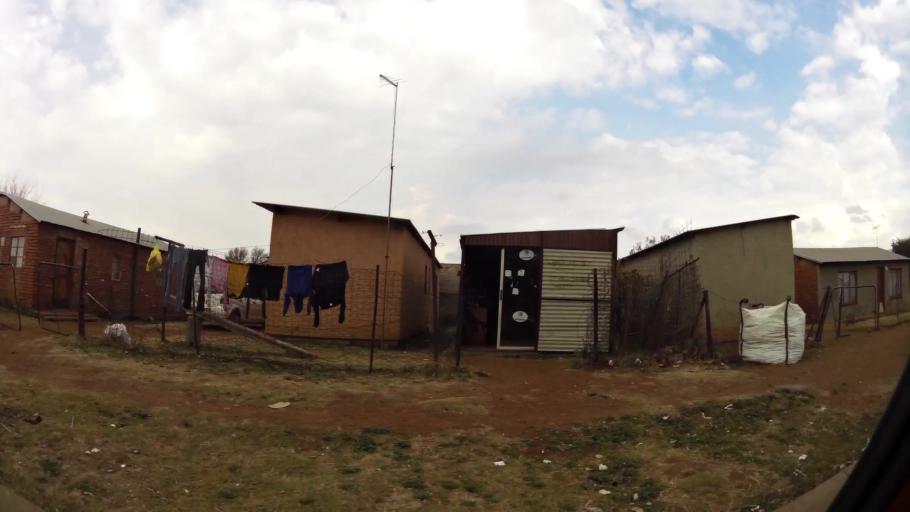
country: ZA
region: Gauteng
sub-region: Sedibeng District Municipality
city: Vanderbijlpark
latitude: -26.6637
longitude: 27.8468
